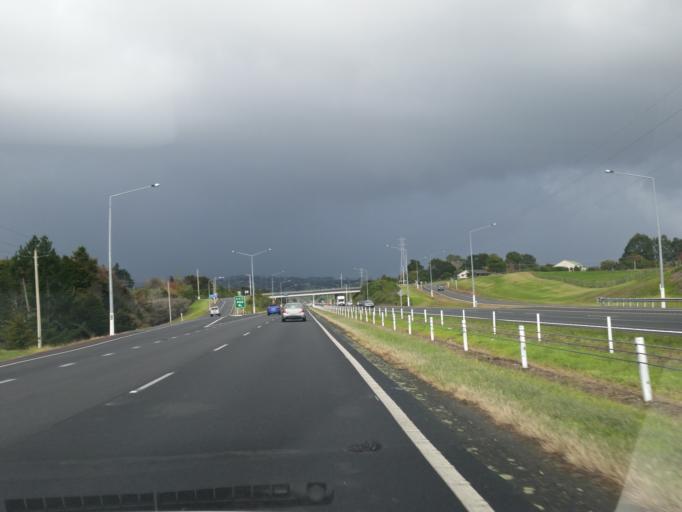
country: NZ
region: Auckland
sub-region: Auckland
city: Pukekohe East
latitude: -37.1405
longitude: 174.9680
